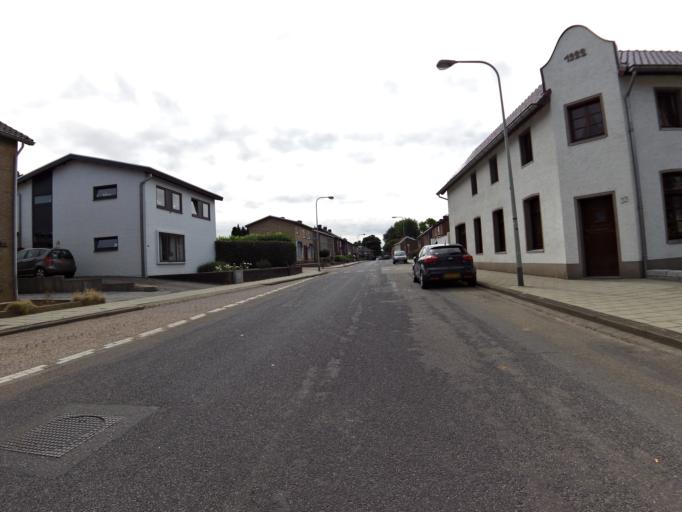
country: NL
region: Limburg
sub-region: Gemeente Onderbanken
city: Merkelbeek
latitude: 50.9563
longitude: 5.9311
